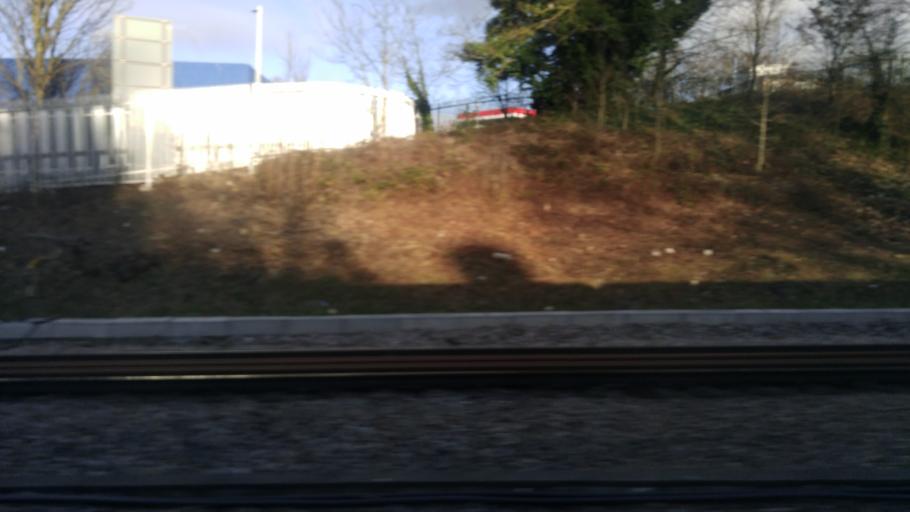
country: GB
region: England
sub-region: Greater London
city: Bromley
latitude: 51.4321
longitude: 0.0201
